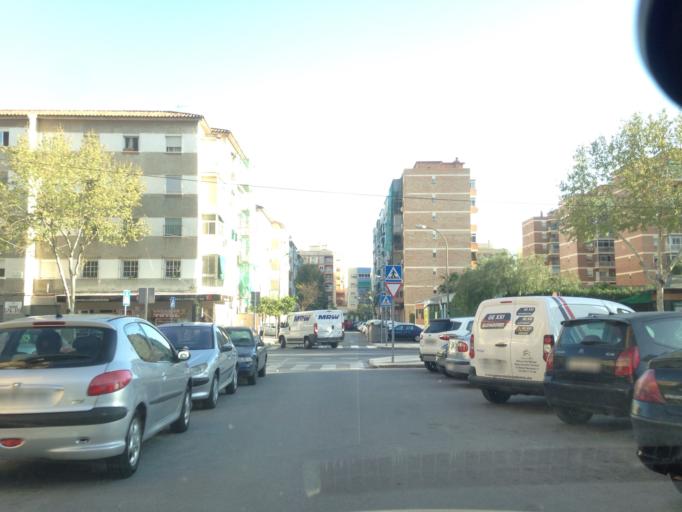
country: ES
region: Andalusia
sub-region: Provincia de Malaga
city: Malaga
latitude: 36.7126
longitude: -4.4482
